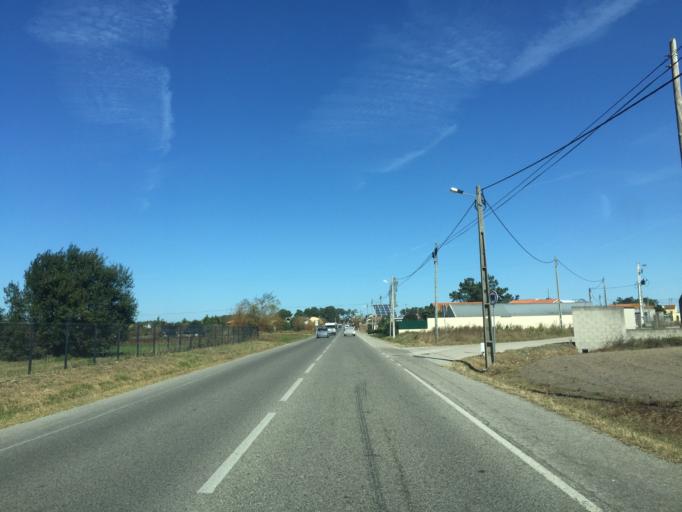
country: PT
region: Coimbra
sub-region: Figueira da Foz
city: Alhadas
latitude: 40.2526
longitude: -8.7832
